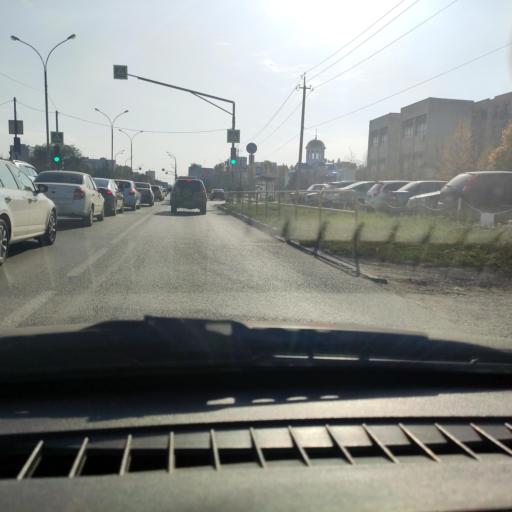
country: RU
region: Samara
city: Tol'yatti
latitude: 53.5367
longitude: 49.3144
